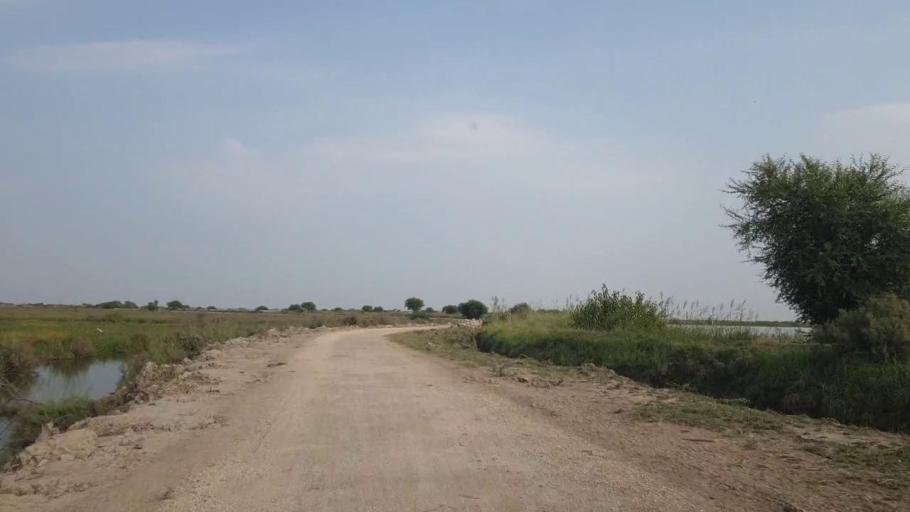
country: PK
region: Sindh
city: Kadhan
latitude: 24.4590
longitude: 68.8061
